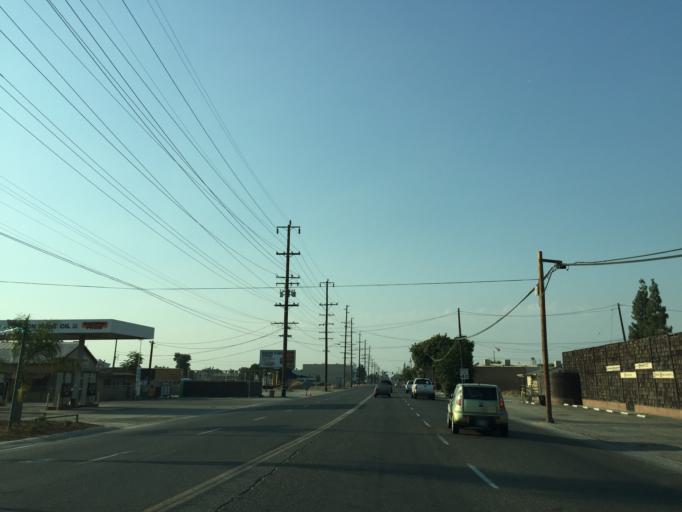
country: US
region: California
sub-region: Tulare County
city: Visalia
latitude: 36.3312
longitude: -119.2787
